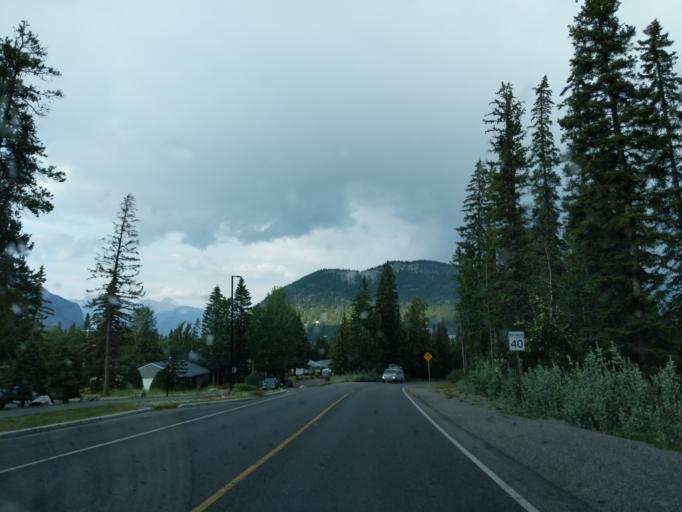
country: CA
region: Alberta
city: Banff
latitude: 51.1676
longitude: -115.5748
